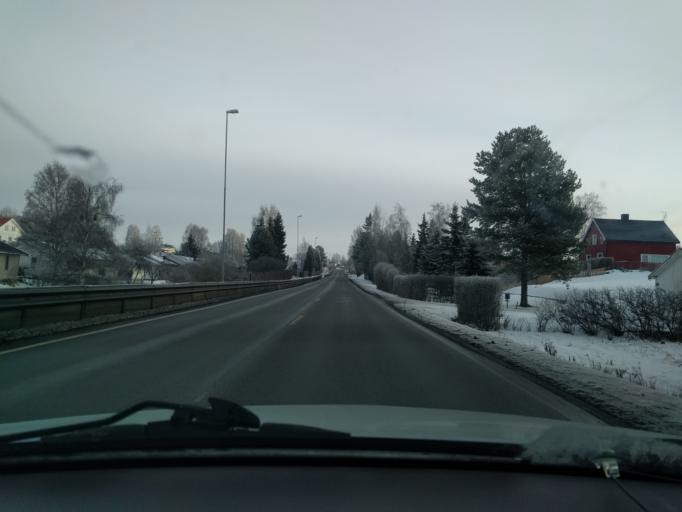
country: NO
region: Hedmark
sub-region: Stange
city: Stange
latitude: 60.8100
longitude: 11.1653
